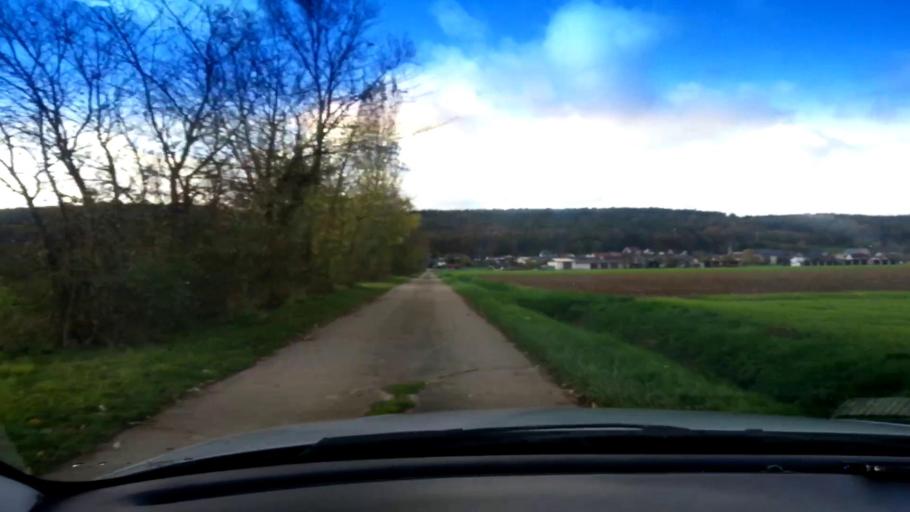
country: DE
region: Bavaria
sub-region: Upper Franconia
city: Zapfendorf
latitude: 50.0453
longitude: 10.9322
